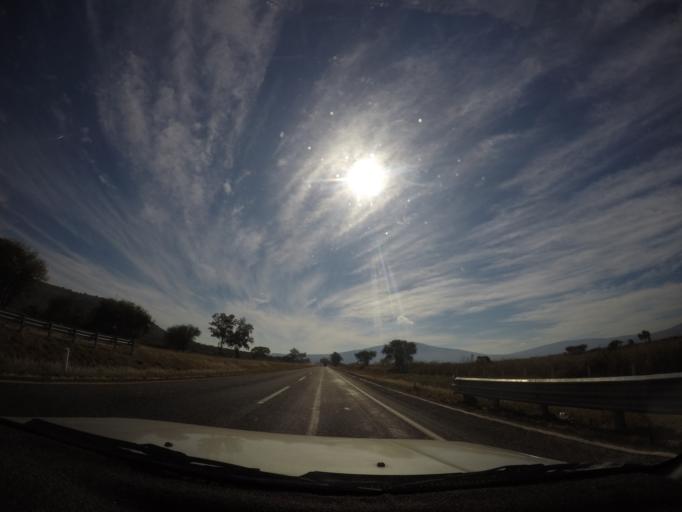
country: MX
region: Jalisco
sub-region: Zapotlanejo
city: La Mezquitera
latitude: 20.5496
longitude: -103.0403
